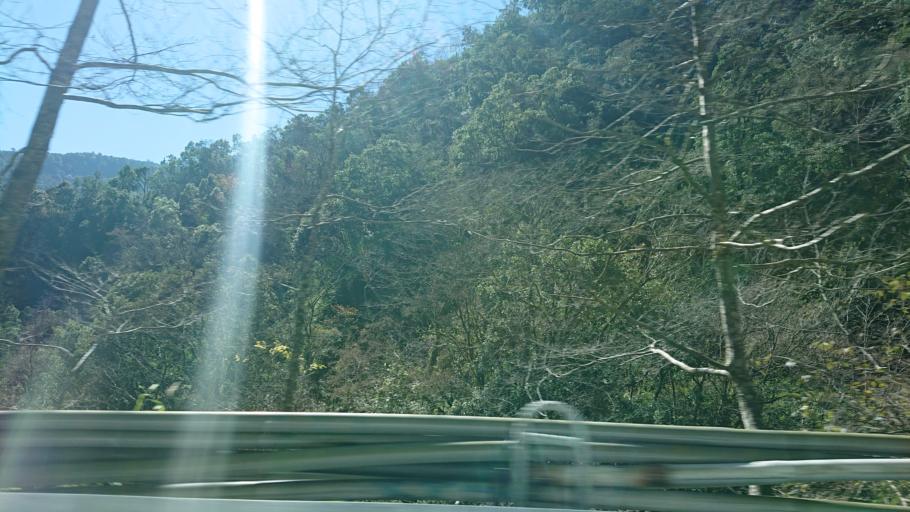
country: TW
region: Taiwan
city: Daxi
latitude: 24.4129
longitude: 121.3587
